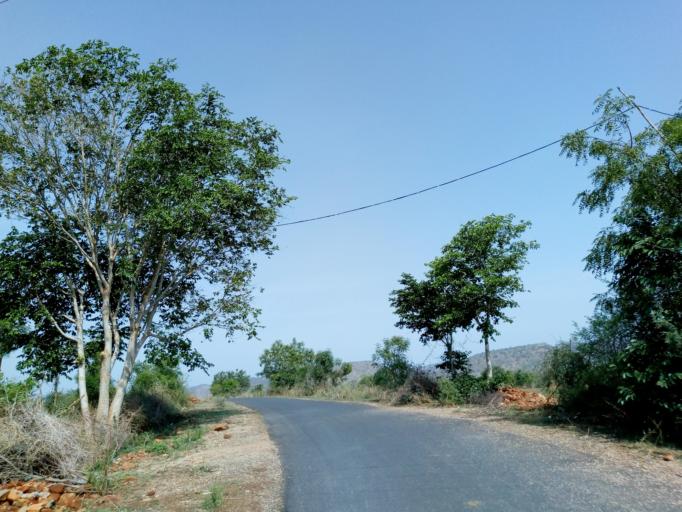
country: IN
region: Andhra Pradesh
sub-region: Prakasam
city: Cumbum
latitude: 15.7145
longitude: 79.0814
